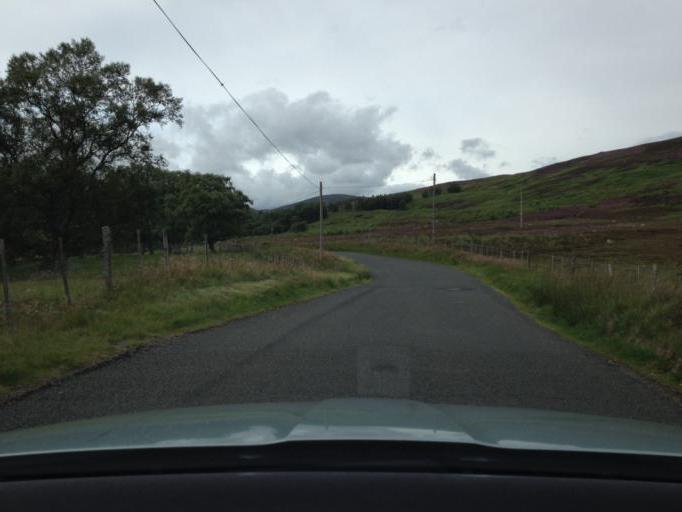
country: GB
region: Scotland
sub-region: Aberdeenshire
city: Aboyne
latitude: 56.9000
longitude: -2.8525
